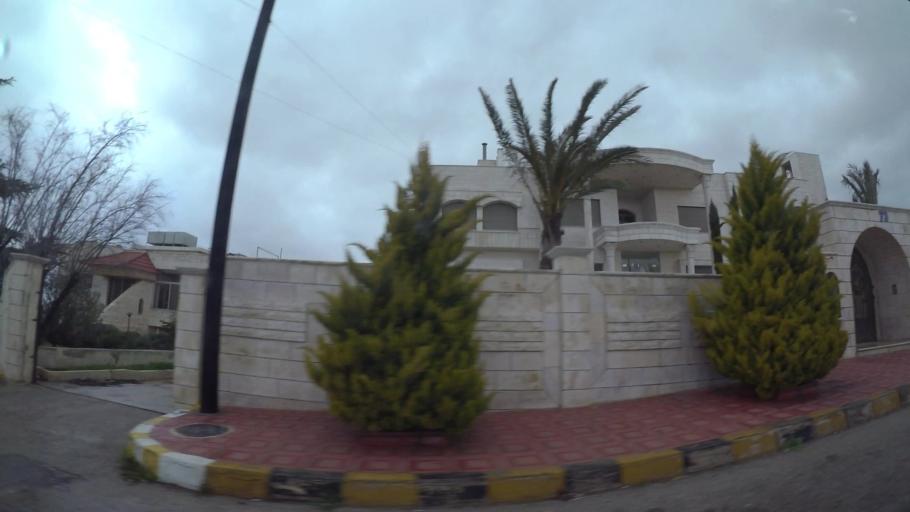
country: JO
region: Amman
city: Al Jubayhah
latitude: 32.0375
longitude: 35.8617
